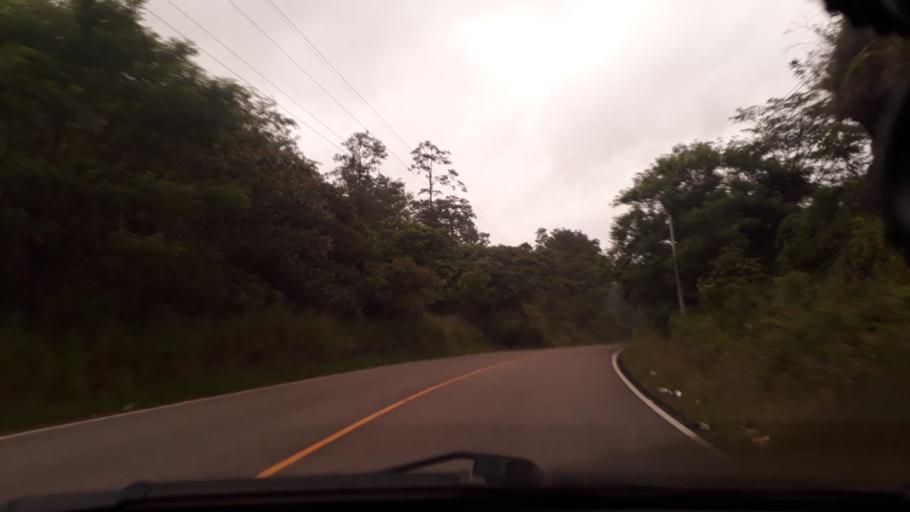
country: GT
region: Chiquimula
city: Esquipulas
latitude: 14.5513
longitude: -89.2919
